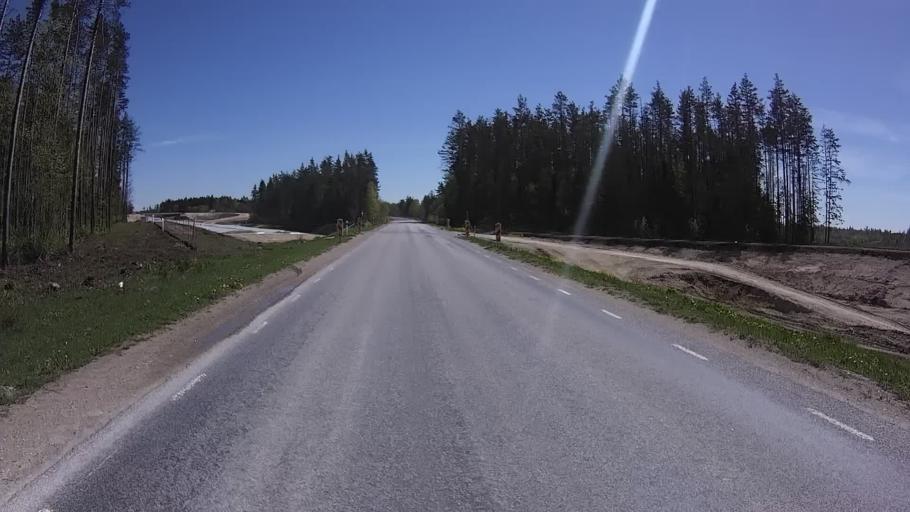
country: EE
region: Harju
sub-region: Raasiku vald
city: Raasiku
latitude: 59.1611
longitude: 25.1820
